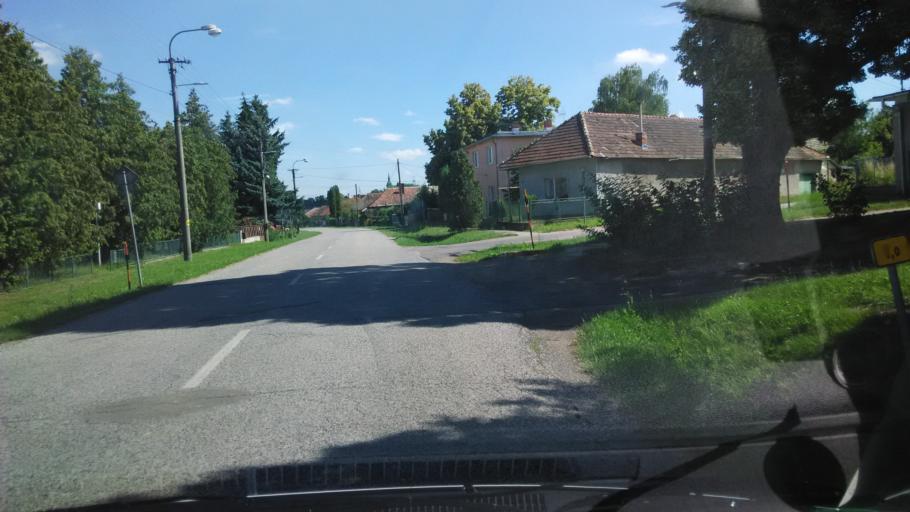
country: SK
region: Nitriansky
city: Tlmace
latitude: 48.2060
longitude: 18.4465
